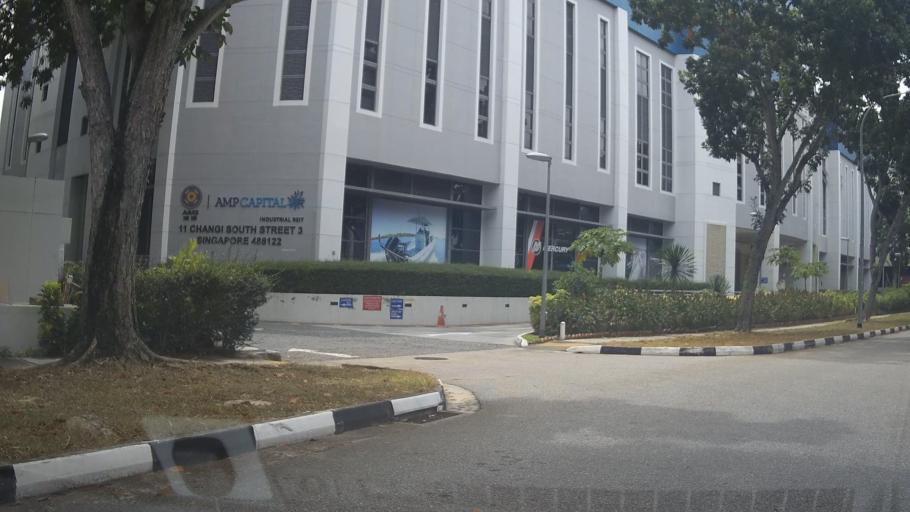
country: SG
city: Singapore
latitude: 1.3288
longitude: 103.9670
